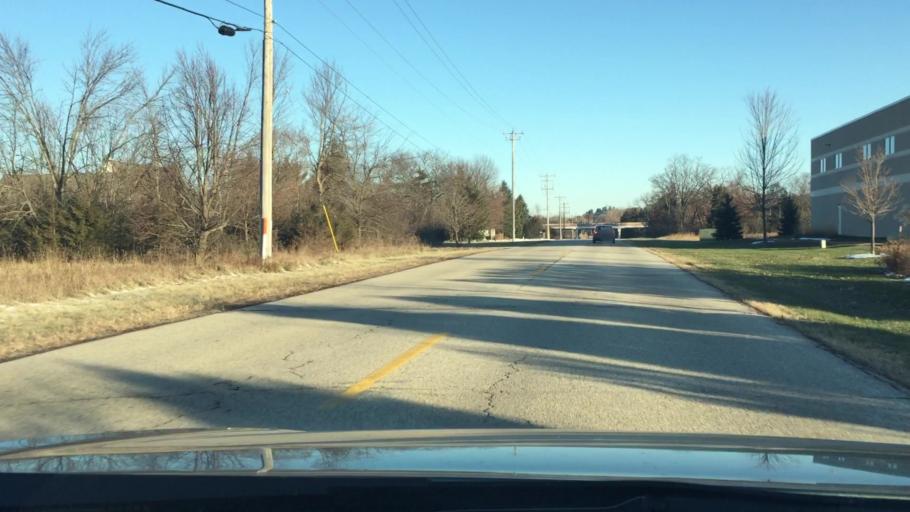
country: US
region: Wisconsin
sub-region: Waukesha County
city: Oconomowoc
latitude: 43.0661
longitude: -88.4812
